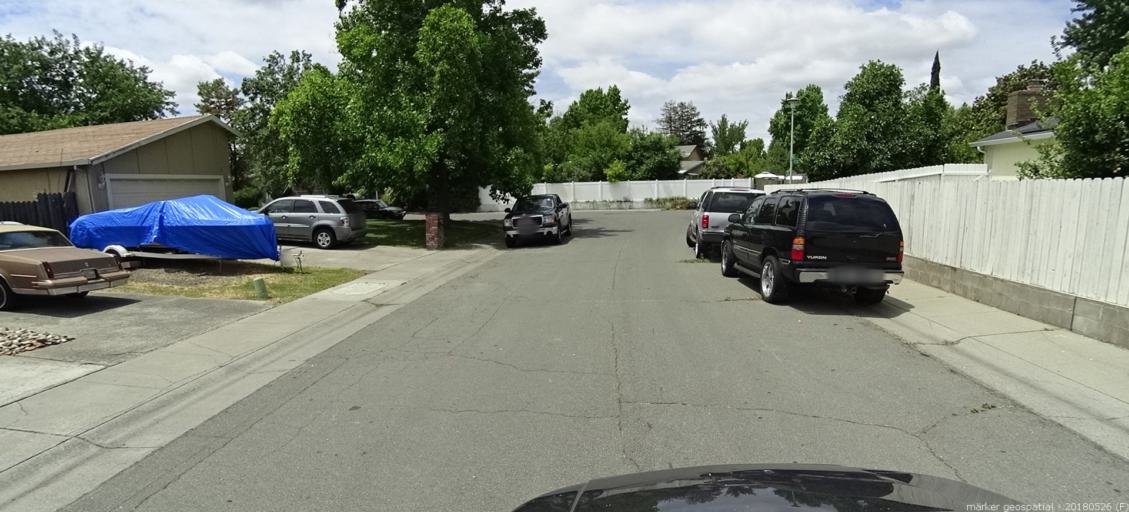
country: US
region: California
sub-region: Sacramento County
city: Sacramento
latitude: 38.6182
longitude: -121.4936
